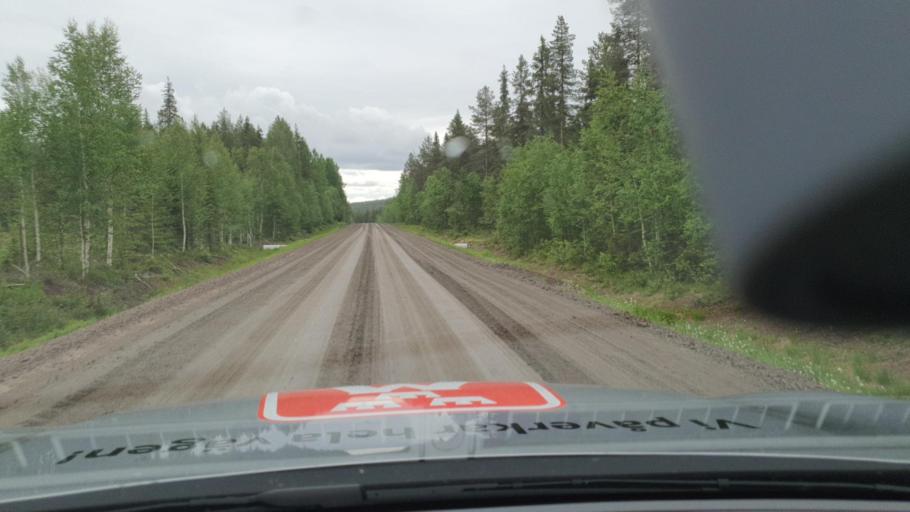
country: SE
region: Norrbotten
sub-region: Overtornea Kommun
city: OEvertornea
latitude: 66.4308
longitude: 23.5224
